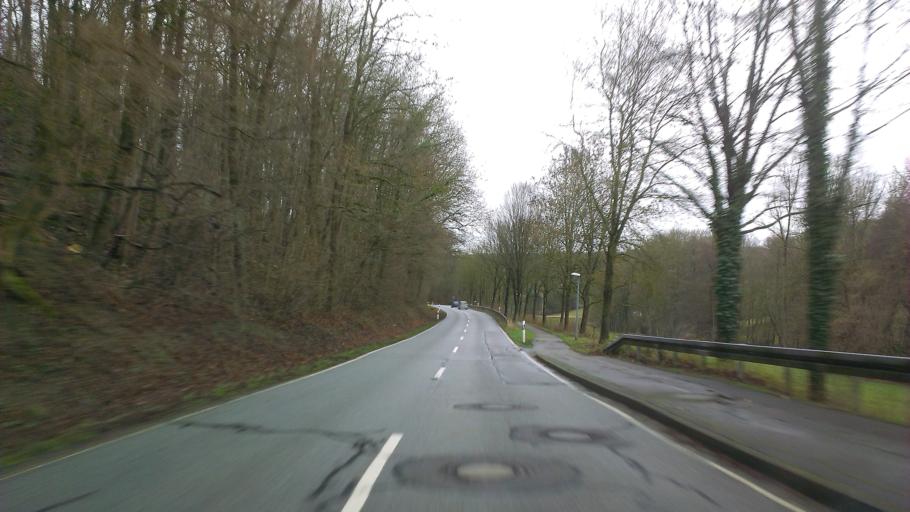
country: DE
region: Baden-Wuerttemberg
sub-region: Regierungsbezirk Stuttgart
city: Zaberfeld
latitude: 49.0721
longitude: 8.8960
